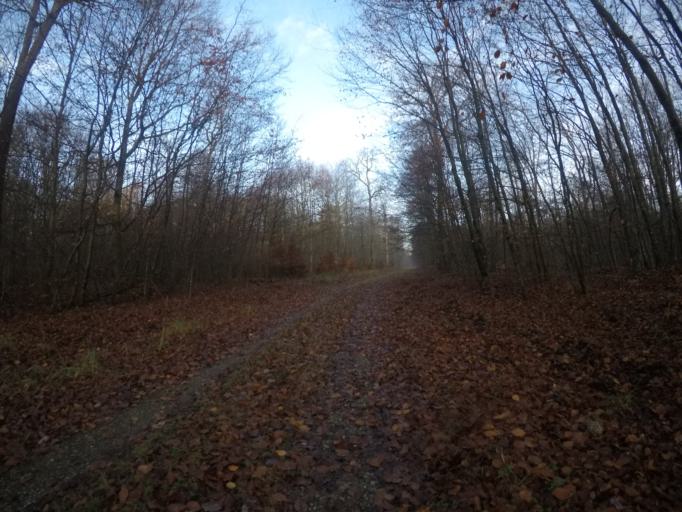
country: BE
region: Wallonia
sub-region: Province du Luxembourg
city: Habay-la-Vieille
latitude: 49.7526
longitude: 5.6708
